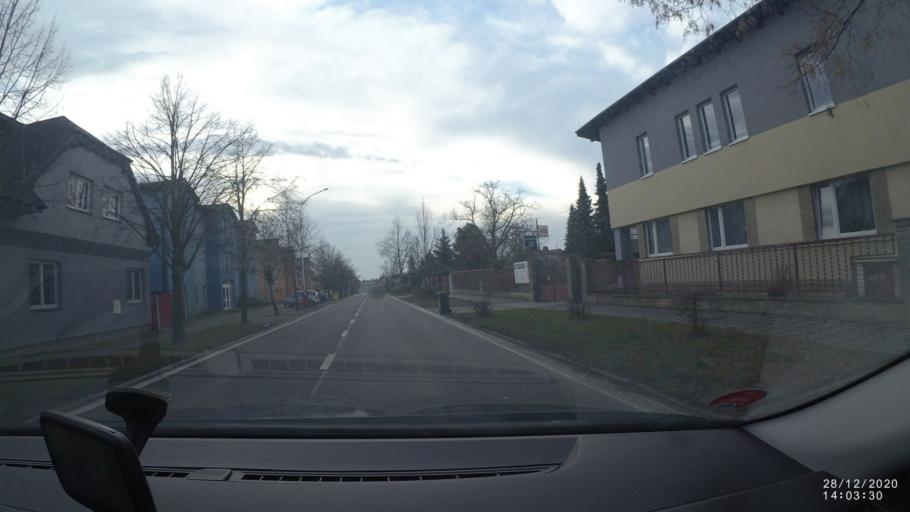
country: CZ
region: Central Bohemia
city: Sestajovice
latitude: 50.1040
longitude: 14.6782
